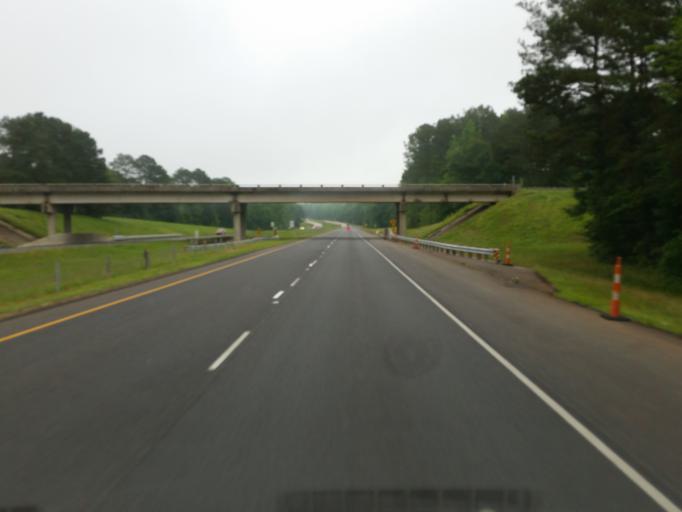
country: US
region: Louisiana
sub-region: Webster Parish
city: Minden
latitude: 32.5631
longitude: -93.1603
